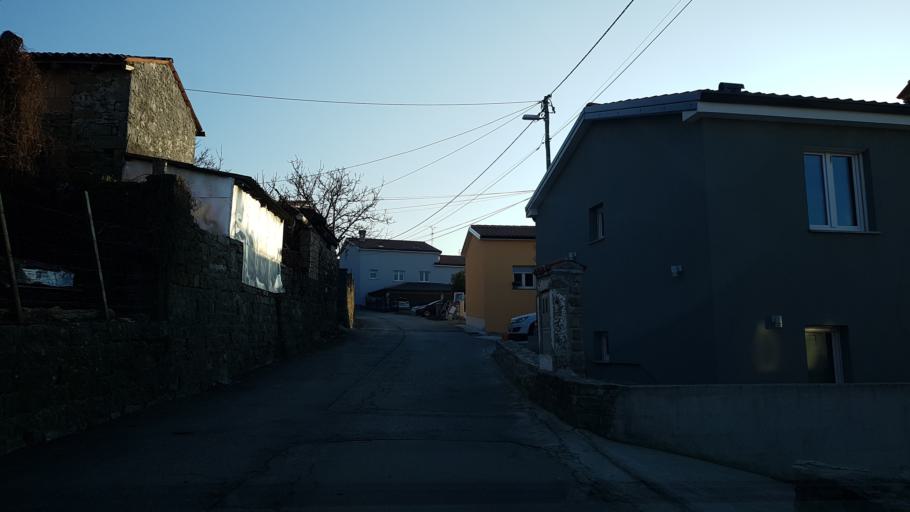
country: SI
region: Koper-Capodistria
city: Sv. Anton
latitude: 45.4865
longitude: 13.7980
